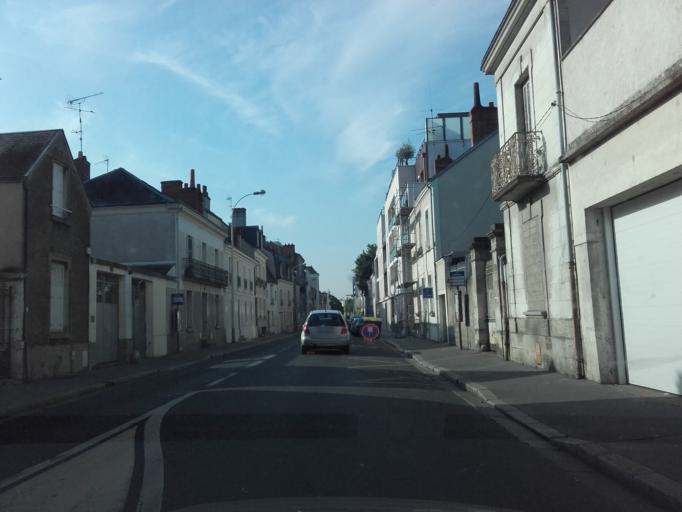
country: FR
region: Centre
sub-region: Departement d'Indre-et-Loire
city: La Riche
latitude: 47.3926
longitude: 0.6725
